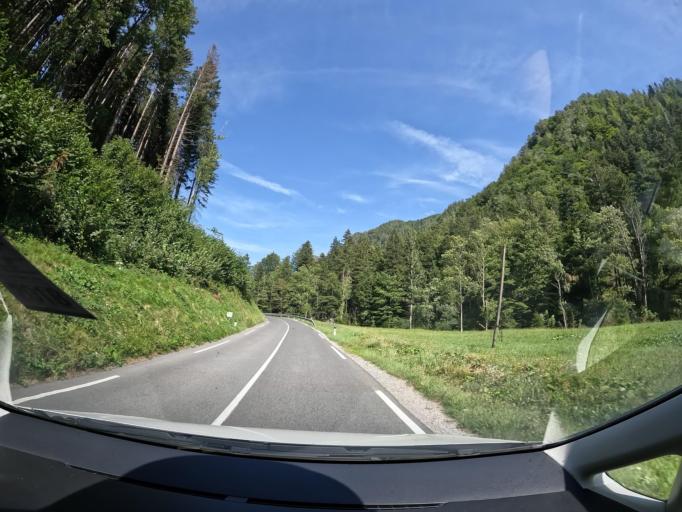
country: SI
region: Zirovnica
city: Zirovnica
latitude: 46.4426
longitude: 14.1794
